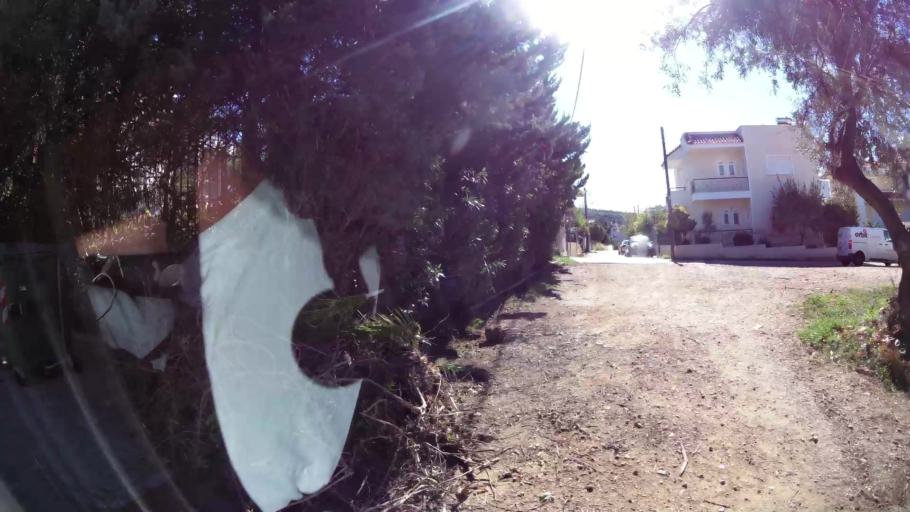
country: GR
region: Attica
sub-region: Nomarchia Anatolikis Attikis
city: Vari
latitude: 37.8338
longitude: 23.8233
